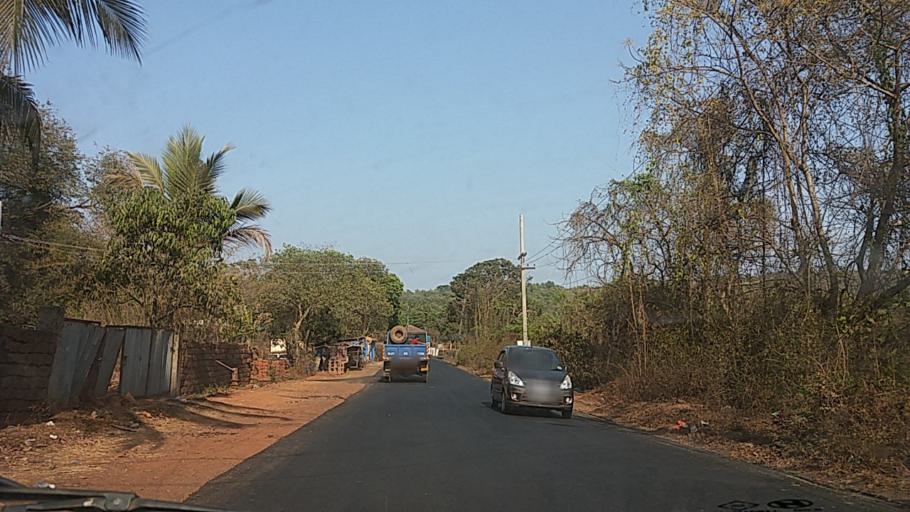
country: IN
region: Goa
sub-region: South Goa
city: Raia
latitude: 15.3073
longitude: 73.9723
